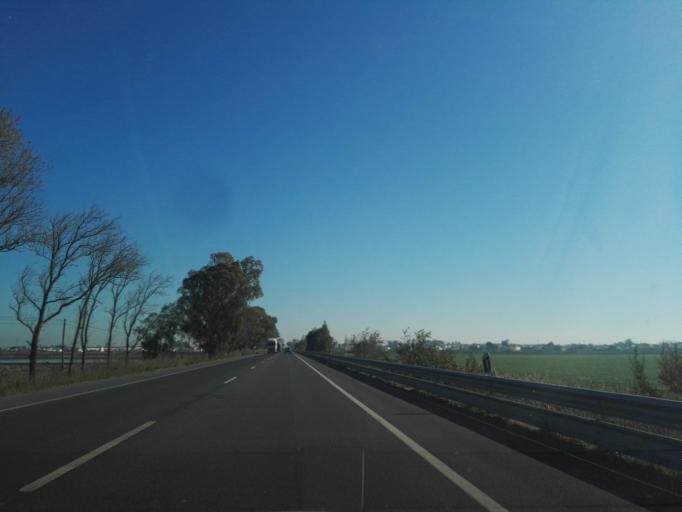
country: PT
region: Santarem
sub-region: Benavente
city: Samora Correia
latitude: 38.9275
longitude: -8.9001
